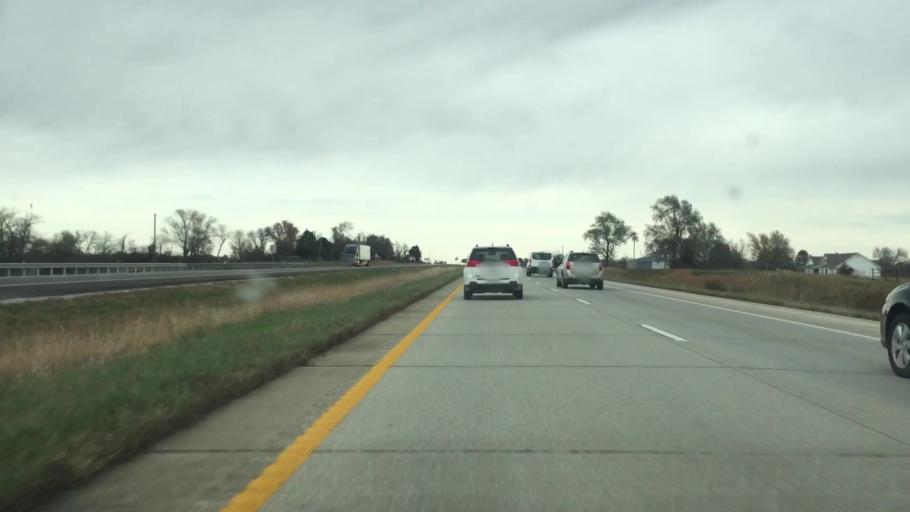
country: US
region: Missouri
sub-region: Saint Clair County
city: Osceola
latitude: 38.1041
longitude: -93.7067
